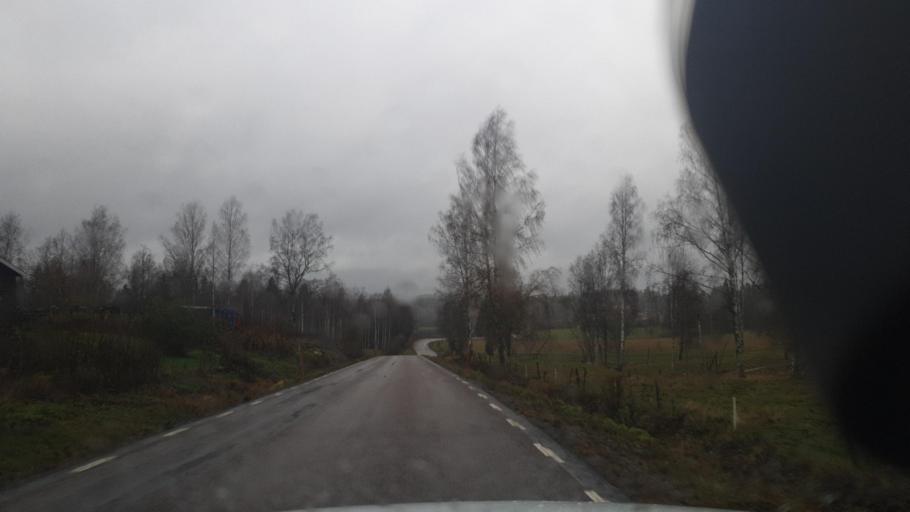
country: SE
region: Vaermland
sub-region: Eda Kommun
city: Charlottenberg
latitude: 59.7624
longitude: 12.2116
